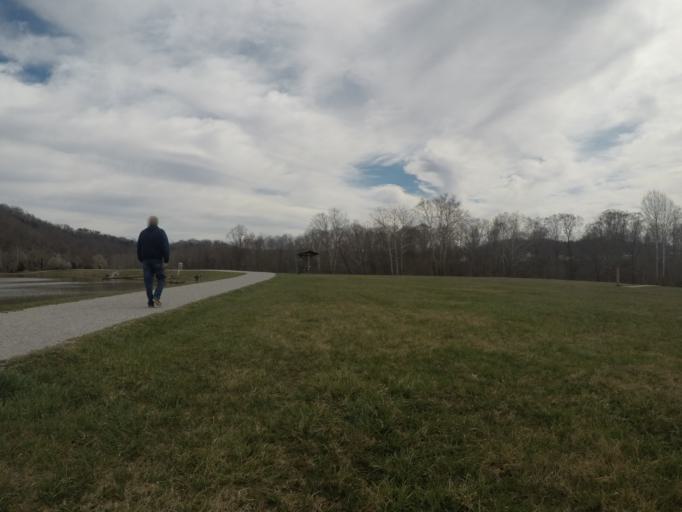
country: US
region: West Virginia
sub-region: Cabell County
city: Barboursville
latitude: 38.3861
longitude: -82.2991
